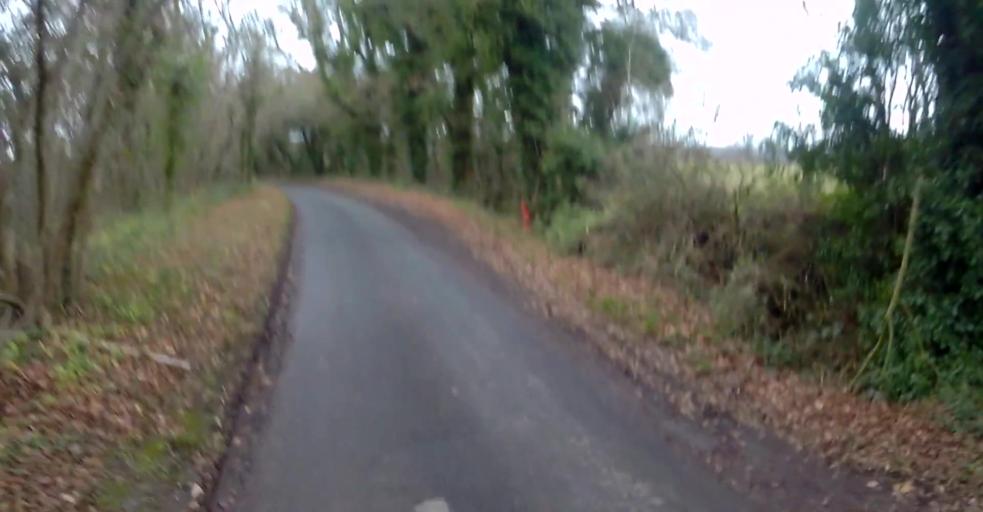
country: GB
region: England
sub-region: Hampshire
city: Overton
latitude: 51.2167
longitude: -1.2155
